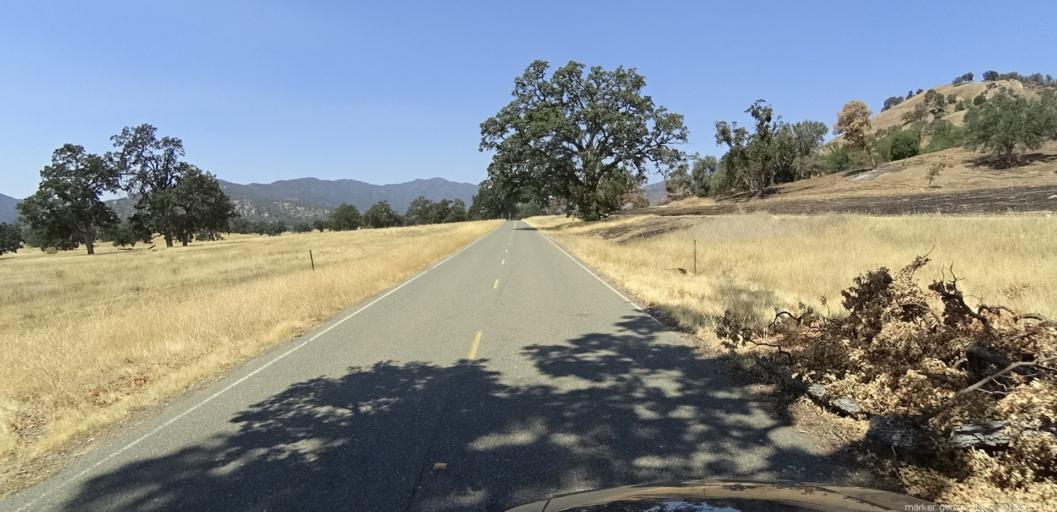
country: US
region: California
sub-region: Monterey County
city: King City
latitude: 35.9634
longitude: -121.2954
